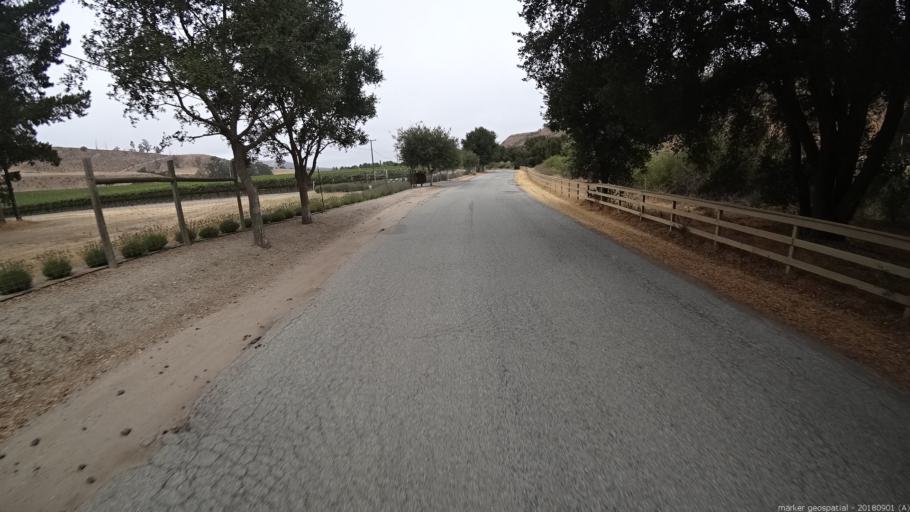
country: US
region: California
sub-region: Monterey County
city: Greenfield
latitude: 36.2730
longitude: -121.3018
